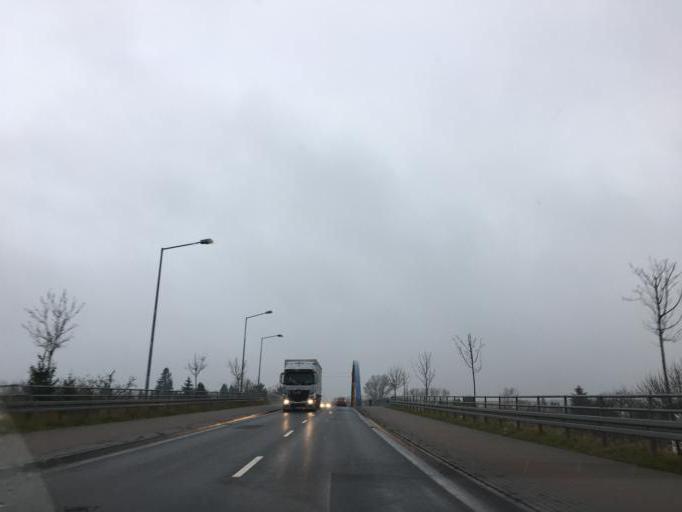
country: DE
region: Saxony-Anhalt
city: Haldensleben I
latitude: 52.2836
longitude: 11.4004
